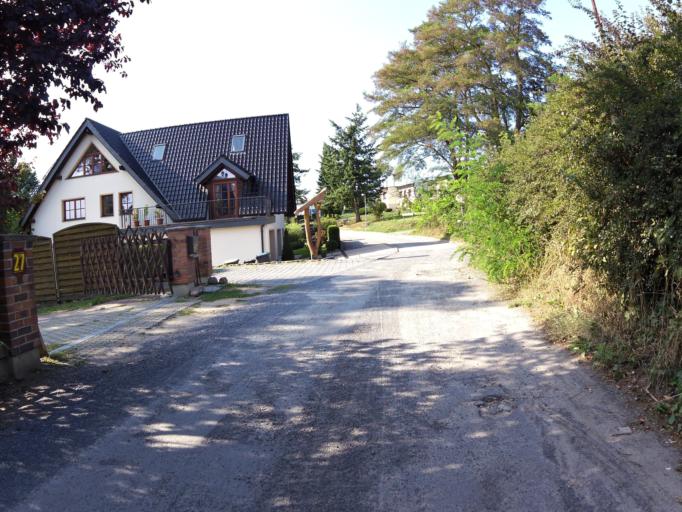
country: DE
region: Mecklenburg-Vorpommern
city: Seebad Bansin
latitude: 53.9601
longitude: 14.1359
